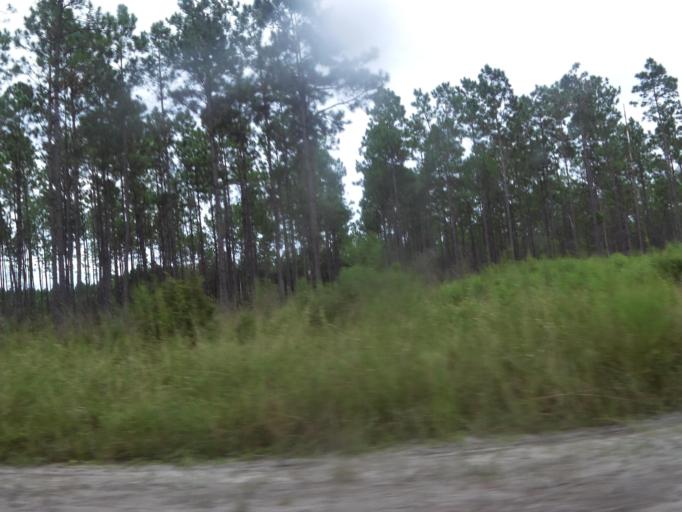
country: US
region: Florida
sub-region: Flagler County
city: Palm Coast
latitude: 29.6099
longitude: -81.3635
